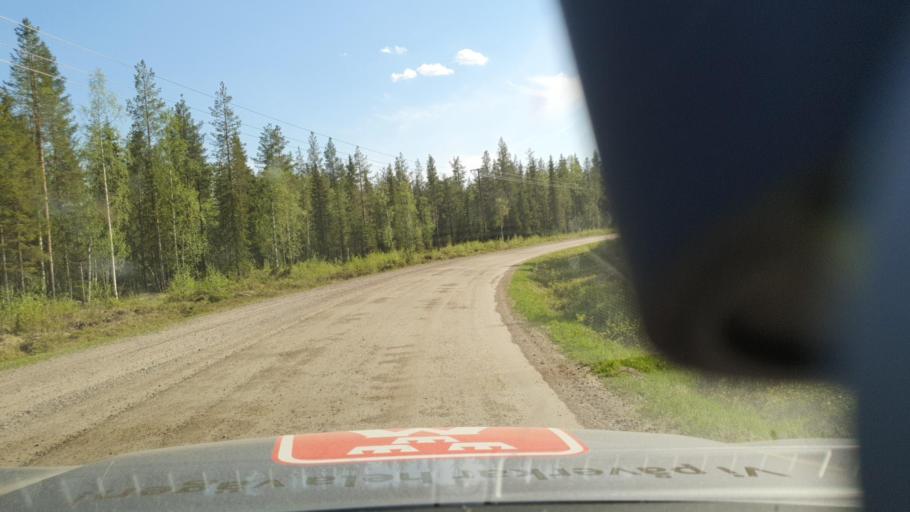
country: SE
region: Norrbotten
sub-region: Bodens Kommun
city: Boden
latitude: 66.3548
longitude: 21.5081
